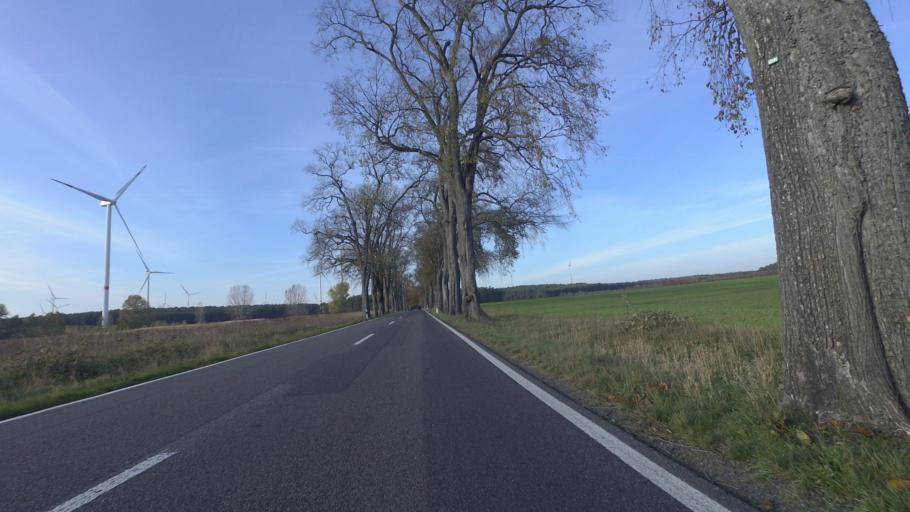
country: DE
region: Brandenburg
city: Sperenberg
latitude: 52.1960
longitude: 13.3151
